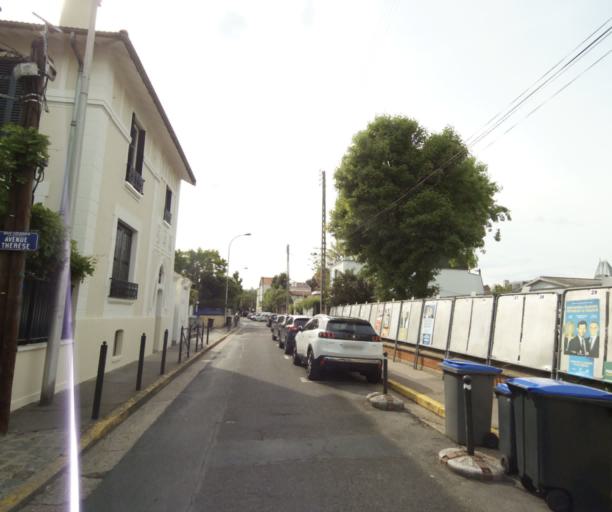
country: FR
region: Ile-de-France
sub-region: Departement des Hauts-de-Seine
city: Colombes
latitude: 48.9160
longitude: 2.2633
